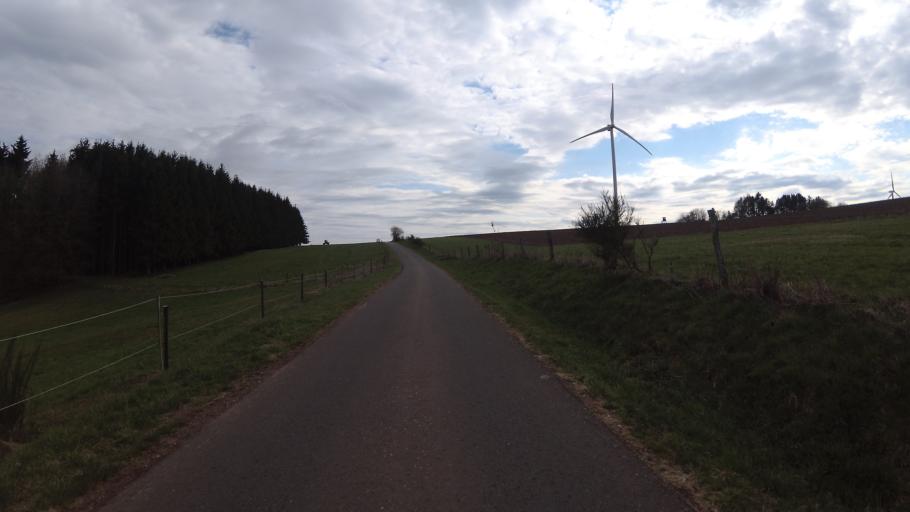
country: DE
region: Rheinland-Pfalz
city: Hahnweiler
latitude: 49.5670
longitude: 7.2184
